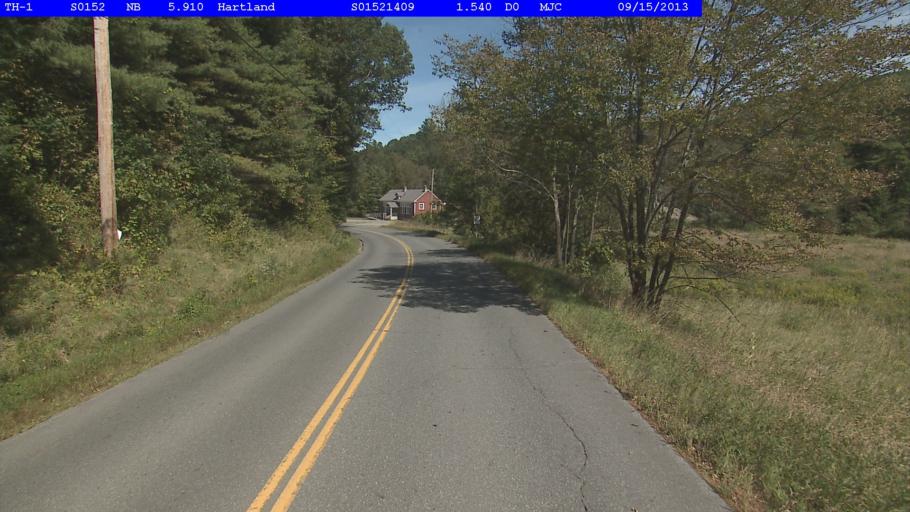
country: US
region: Vermont
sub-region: Windsor County
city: Windsor
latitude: 43.5412
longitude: -72.4275
